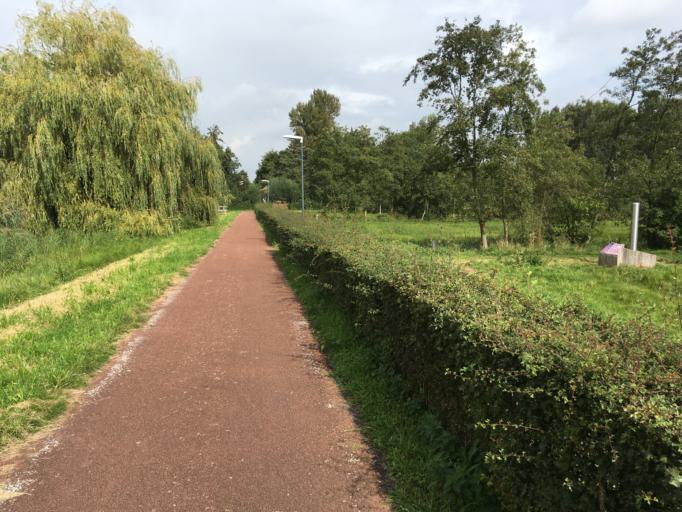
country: NL
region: North Brabant
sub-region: Gemeente Vught
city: Vught
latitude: 51.6394
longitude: 5.2905
